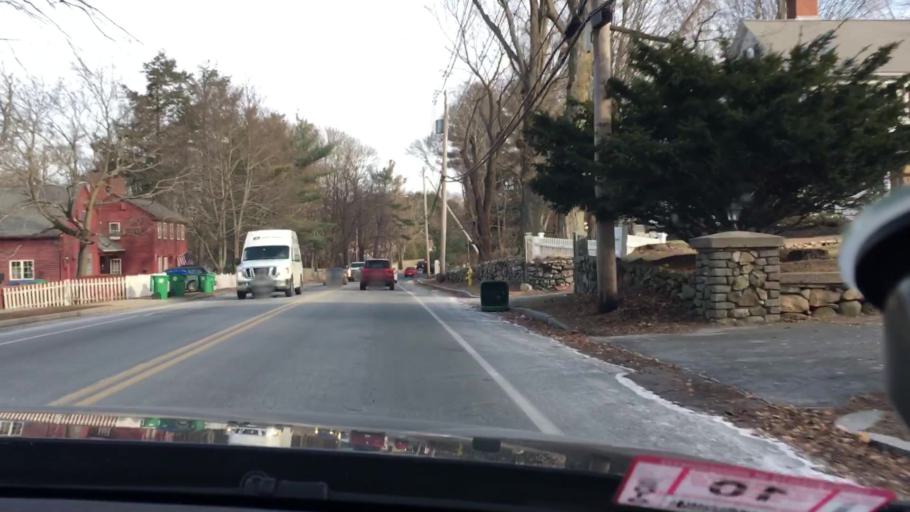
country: US
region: Massachusetts
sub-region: Norfolk County
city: Westwood
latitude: 42.2345
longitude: -71.2187
